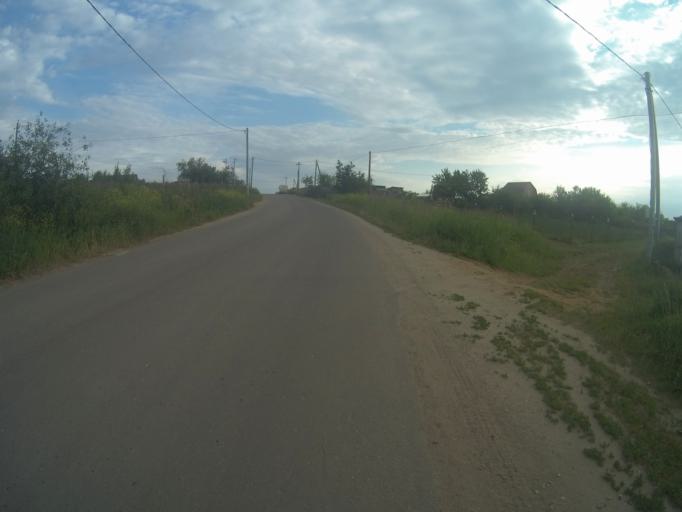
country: RU
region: Vladimir
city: Vladimir
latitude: 56.2141
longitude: 40.4079
